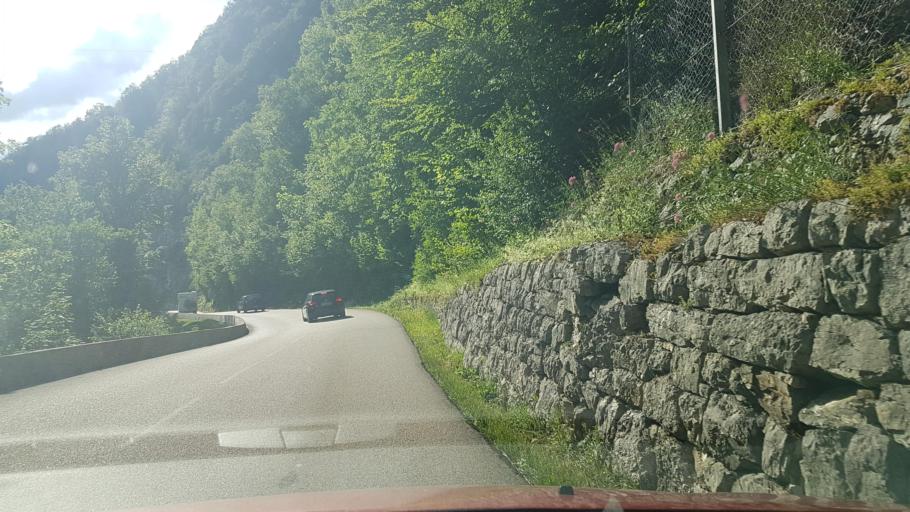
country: FR
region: Franche-Comte
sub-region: Departement du Jura
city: Saint-Claude
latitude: 46.3630
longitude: 5.8934
